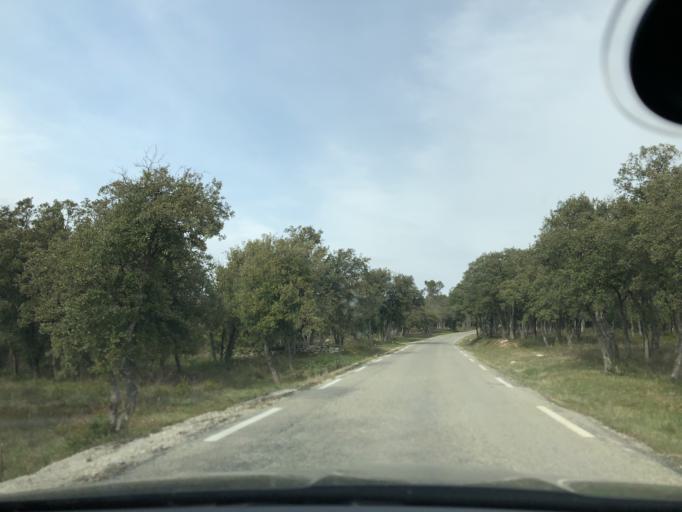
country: FR
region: Provence-Alpes-Cote d'Azur
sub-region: Departement du Vaucluse
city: Menerbes
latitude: 43.8415
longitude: 5.2169
